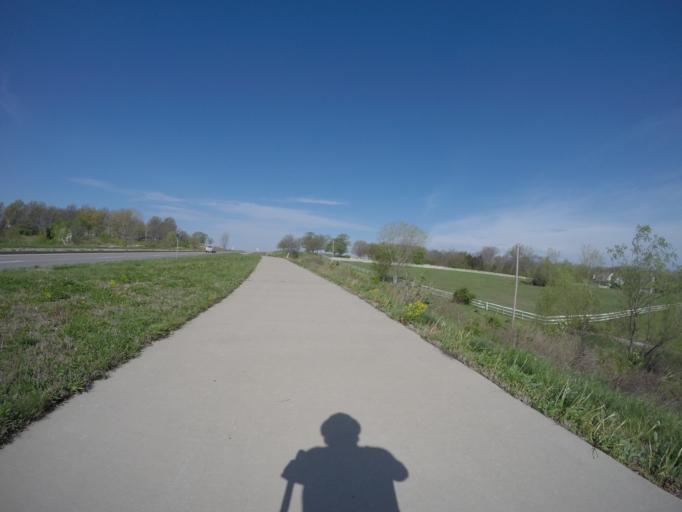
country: US
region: Missouri
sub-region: Jackson County
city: Grandview
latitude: 38.8568
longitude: -94.4846
